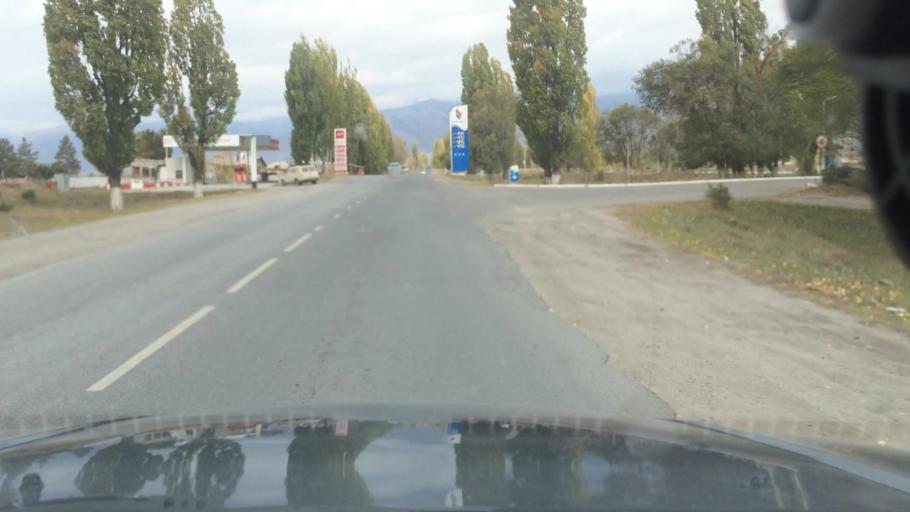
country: KG
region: Ysyk-Koel
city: Tyup
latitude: 42.7394
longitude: 78.3447
